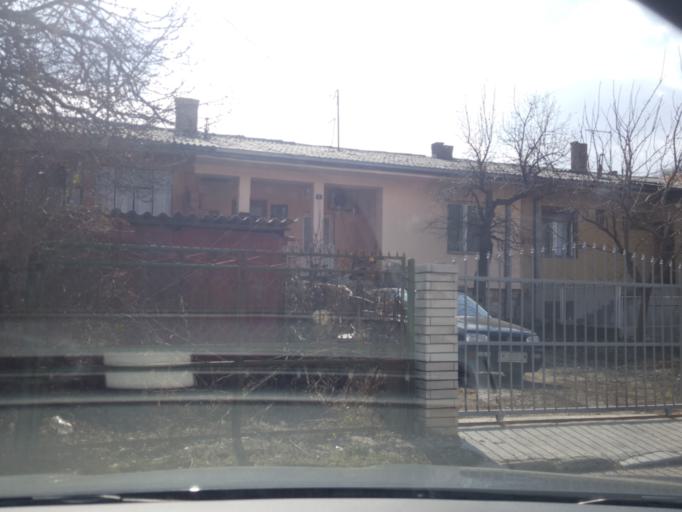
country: RS
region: Central Serbia
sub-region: Nisavski Okrug
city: Nis
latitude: 43.3132
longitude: 21.8672
